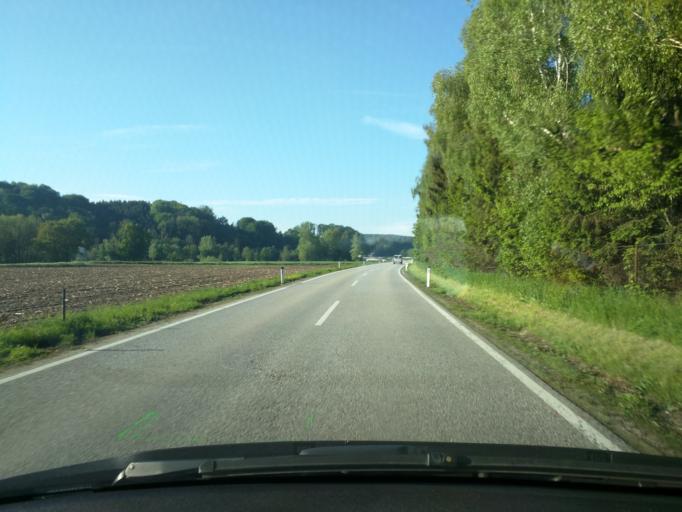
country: AT
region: Lower Austria
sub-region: Politischer Bezirk Melk
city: Blindenmarkt
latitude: 48.1209
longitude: 15.0135
